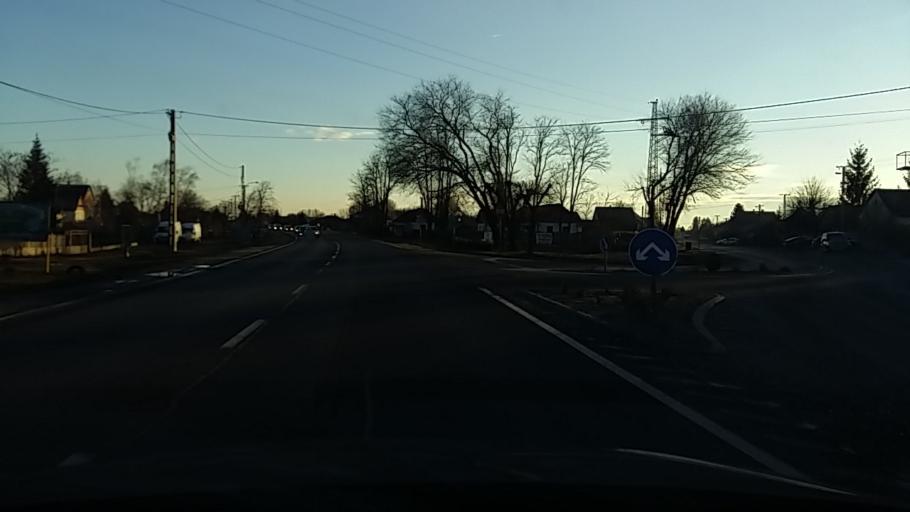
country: HU
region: Szabolcs-Szatmar-Bereg
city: Ujfeherto
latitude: 47.8246
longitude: 21.6985
